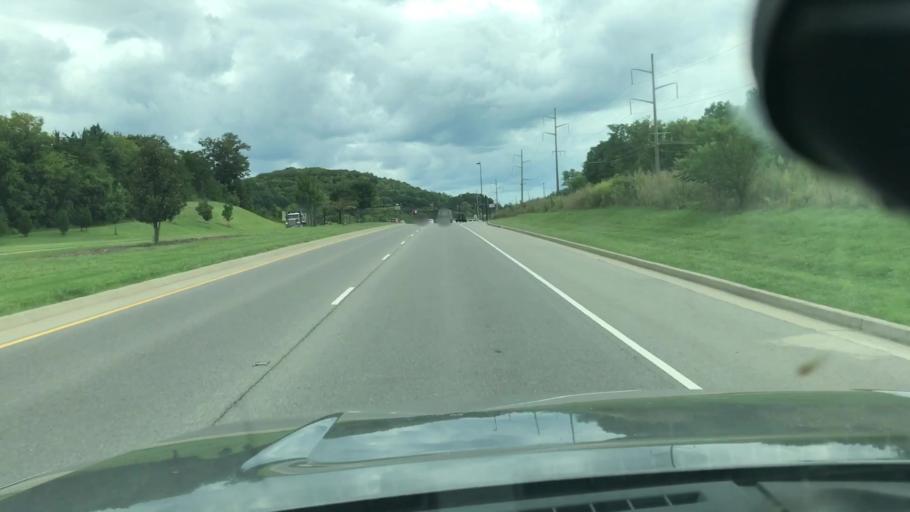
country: US
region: Tennessee
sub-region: Williamson County
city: Franklin
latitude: 35.9269
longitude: -86.8424
